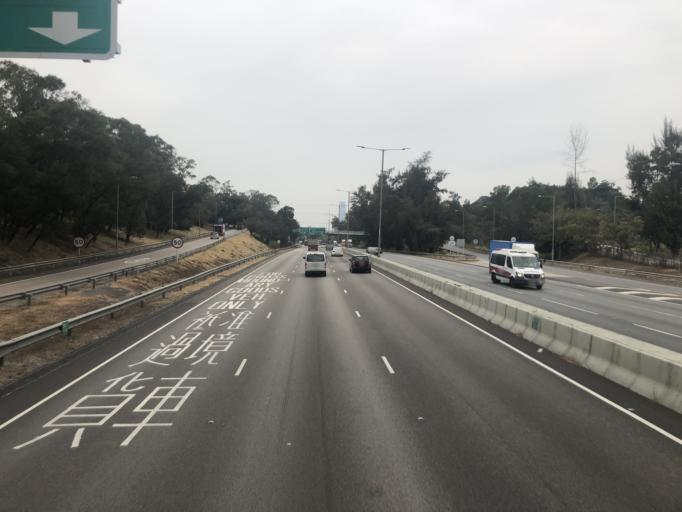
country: CN
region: Guangdong
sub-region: Shenzhen
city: Shenzhen
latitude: 22.5040
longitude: 114.0938
